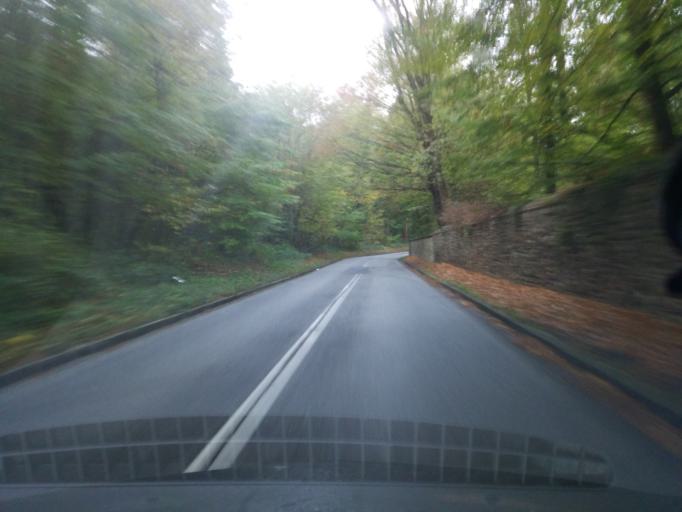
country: FR
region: Ile-de-France
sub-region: Departement de l'Essonne
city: Les Molieres
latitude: 48.6911
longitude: 2.0663
